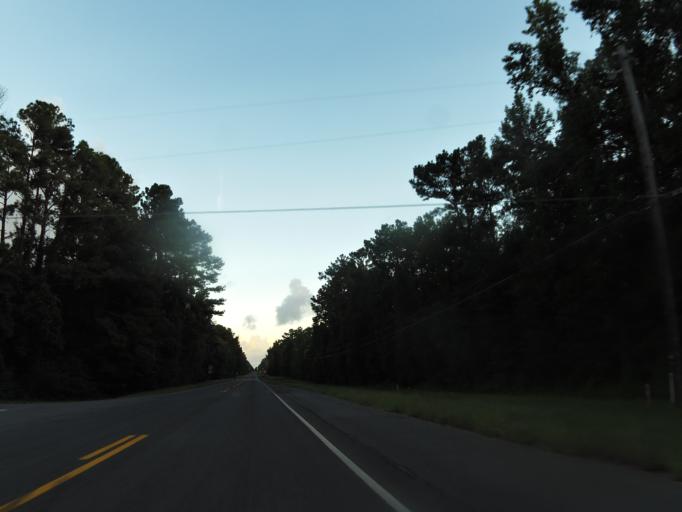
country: US
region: Georgia
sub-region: Camden County
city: Woodbine
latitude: 30.9326
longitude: -81.7166
